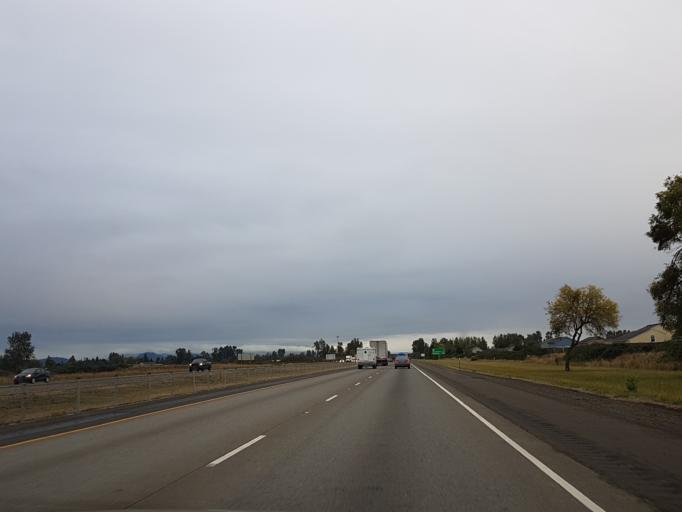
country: US
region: Oregon
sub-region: Linn County
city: Albany
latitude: 44.6192
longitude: -123.0623
